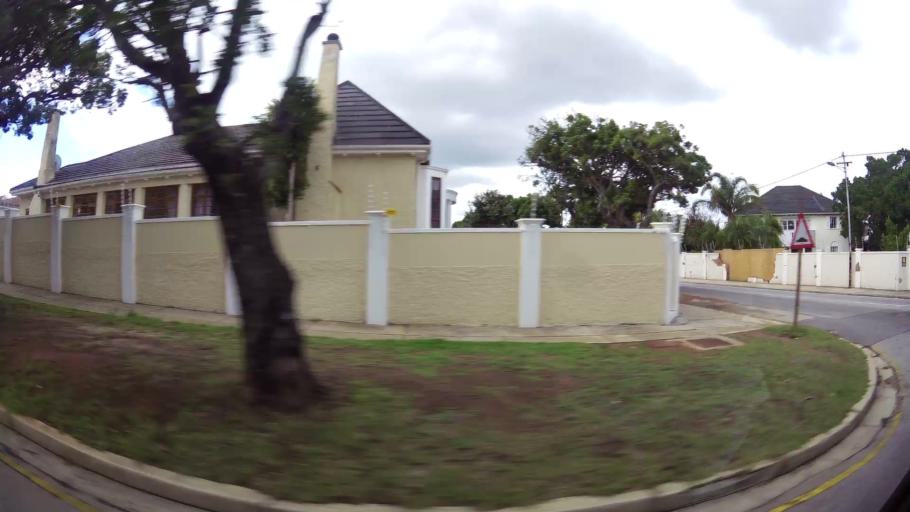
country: ZA
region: Eastern Cape
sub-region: Nelson Mandela Bay Metropolitan Municipality
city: Port Elizabeth
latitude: -33.9582
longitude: 25.5924
